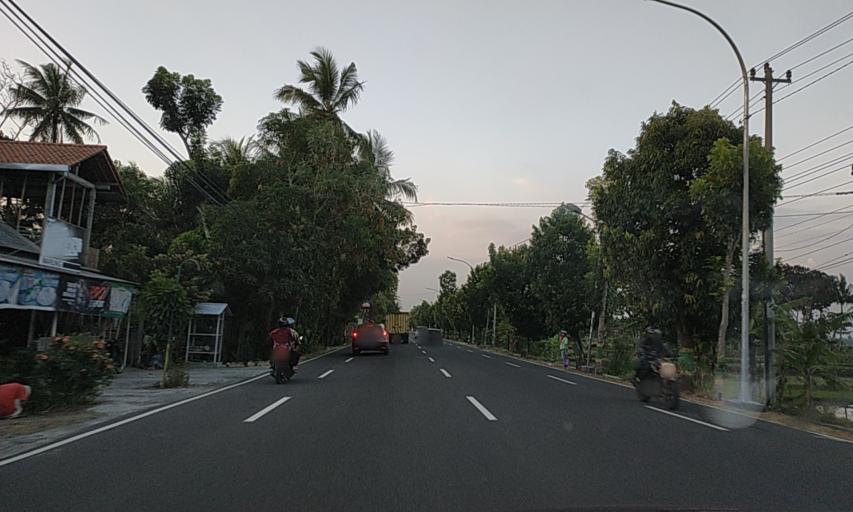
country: ID
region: Daerah Istimewa Yogyakarta
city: Srandakan
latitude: -7.8836
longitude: 110.1313
